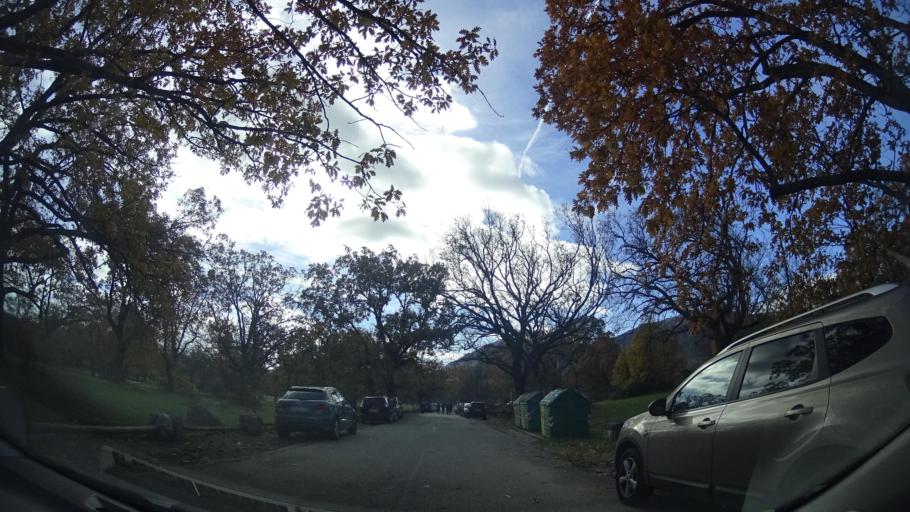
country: ES
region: Madrid
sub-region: Provincia de Madrid
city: San Lorenzo de El Escorial
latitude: 40.5837
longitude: -4.1448
